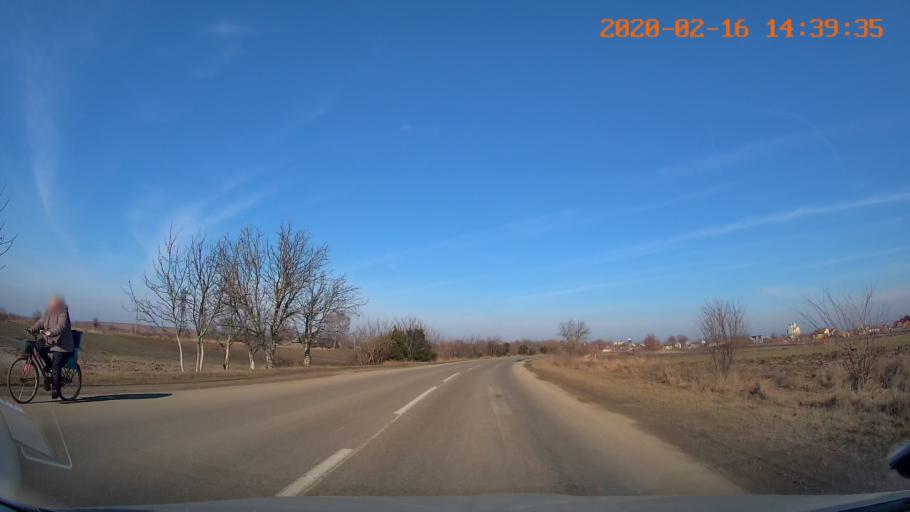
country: RO
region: Botosani
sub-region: Comuna Darabani
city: Bajura
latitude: 48.2448
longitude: 26.5504
